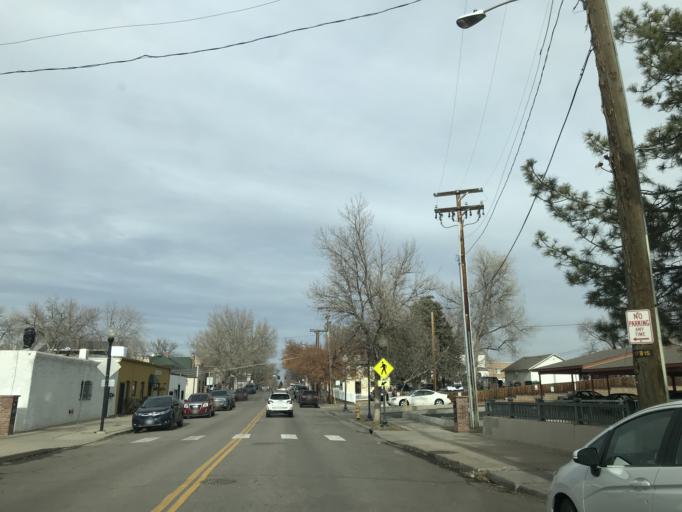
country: US
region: Colorado
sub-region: Arapahoe County
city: Littleton
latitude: 39.6117
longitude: -105.0184
